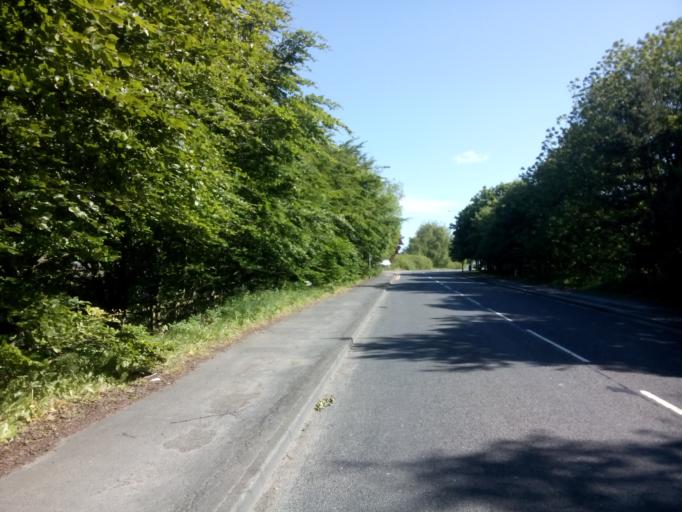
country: GB
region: England
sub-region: County Durham
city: Durham
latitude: 54.7882
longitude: -1.5407
